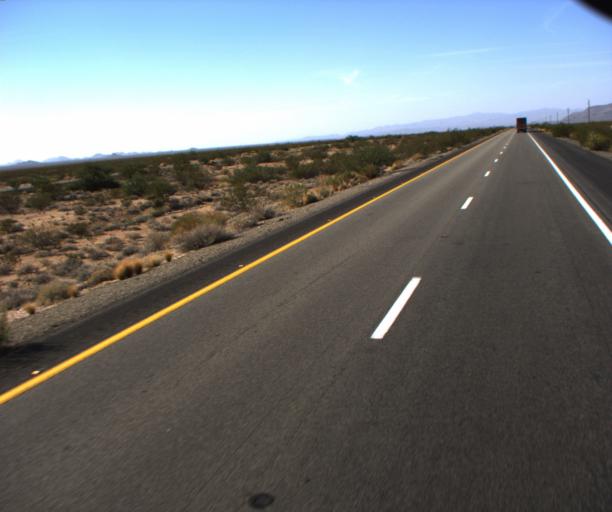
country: US
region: Arizona
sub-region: Mohave County
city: Kingman
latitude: 34.9585
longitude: -114.1448
